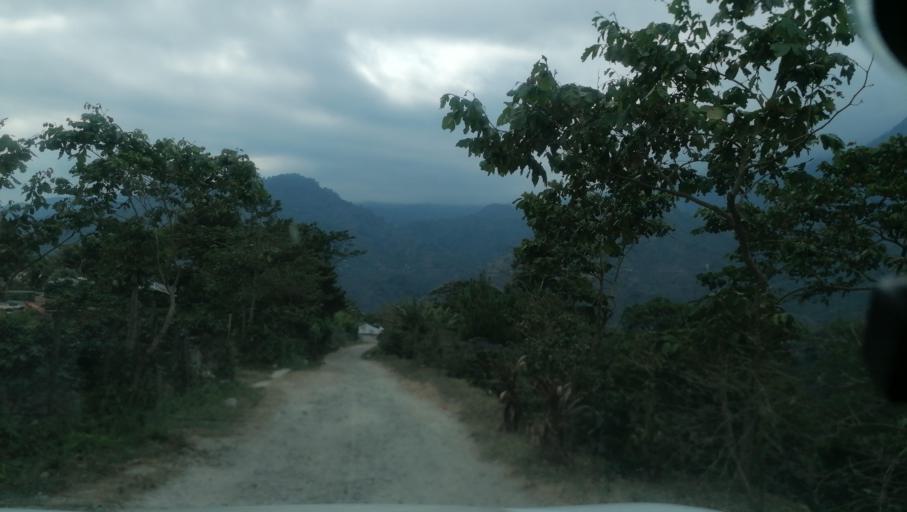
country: MX
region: Chiapas
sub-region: Cacahoatan
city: Benito Juarez
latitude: 15.1702
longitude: -92.1665
